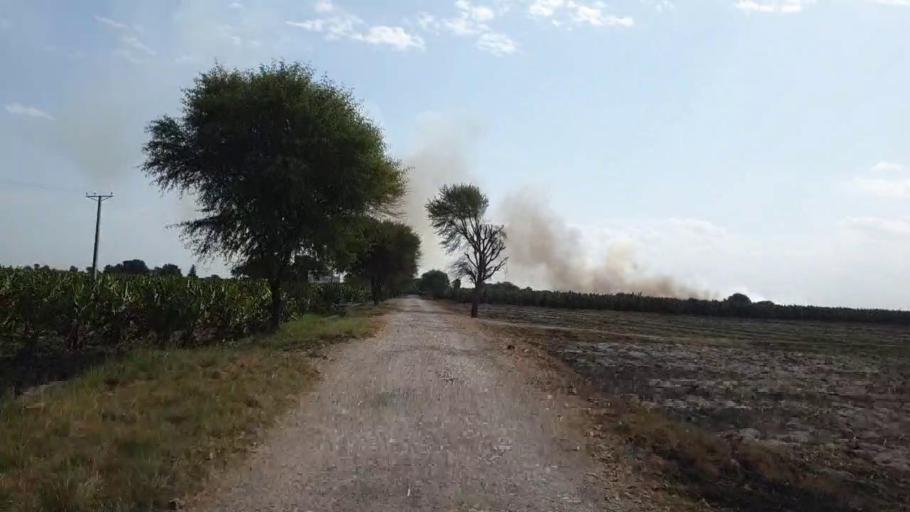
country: PK
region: Sindh
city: Matiari
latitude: 25.5551
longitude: 68.5580
